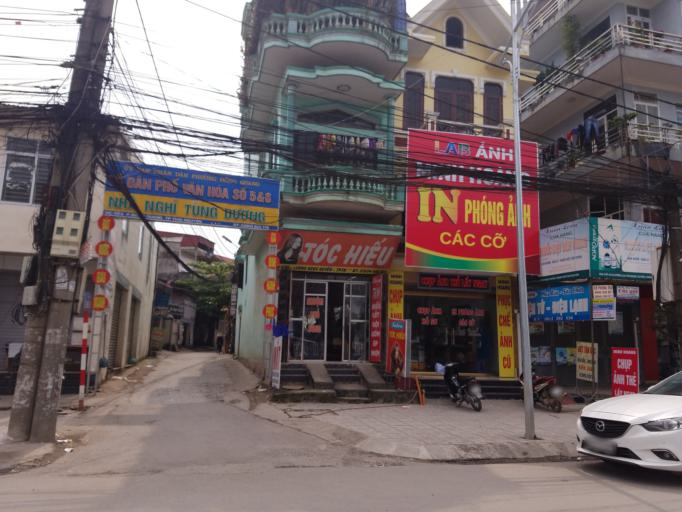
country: VN
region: Thai Nguyen
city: Thanh Pho Thai Nguyen
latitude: 21.5863
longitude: 105.8314
